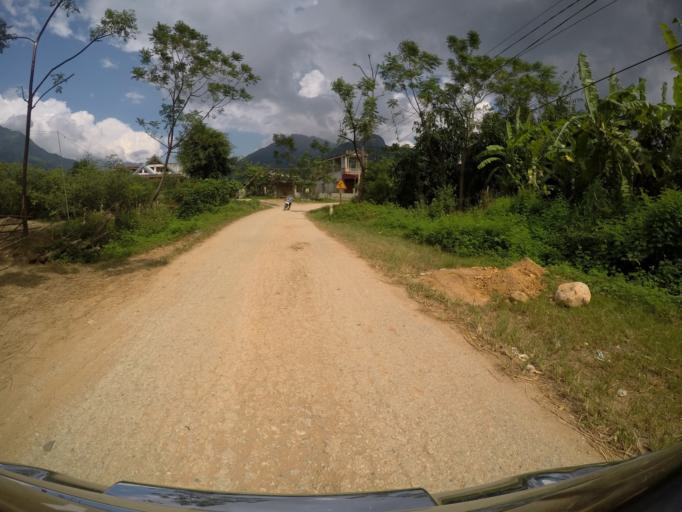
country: VN
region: Yen Bai
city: Son Thinh
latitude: 21.6589
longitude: 104.5035
